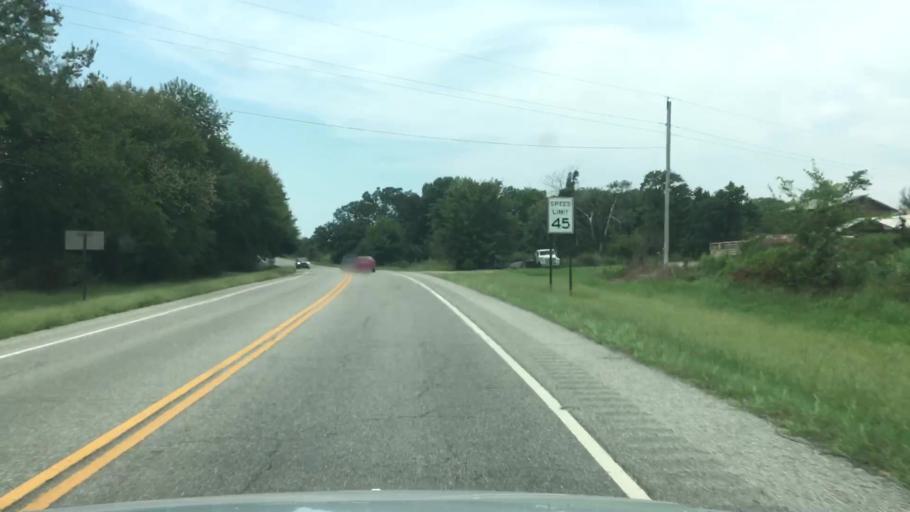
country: US
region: Oklahoma
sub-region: Muskogee County
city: Fort Gibson
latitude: 35.9366
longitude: -95.1636
